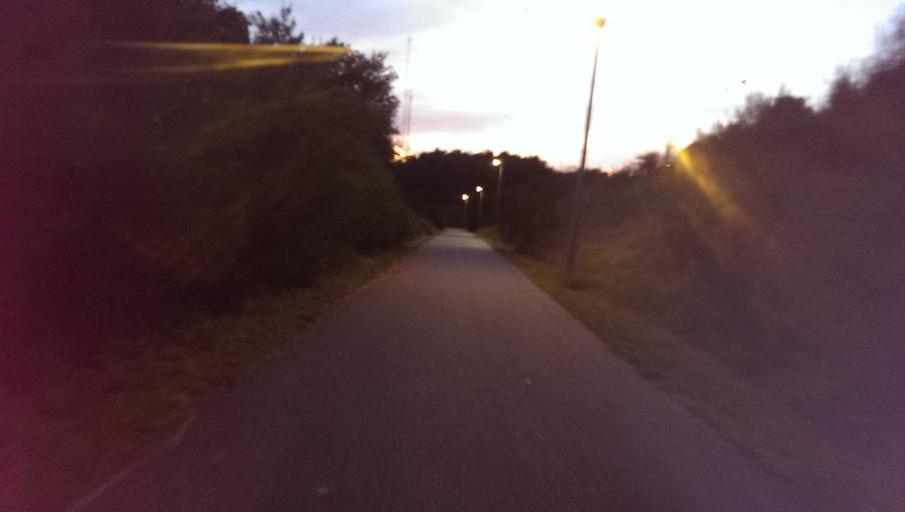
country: DK
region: South Denmark
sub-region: Esbjerg Kommune
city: Tjaereborg
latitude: 55.4665
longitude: 8.5826
